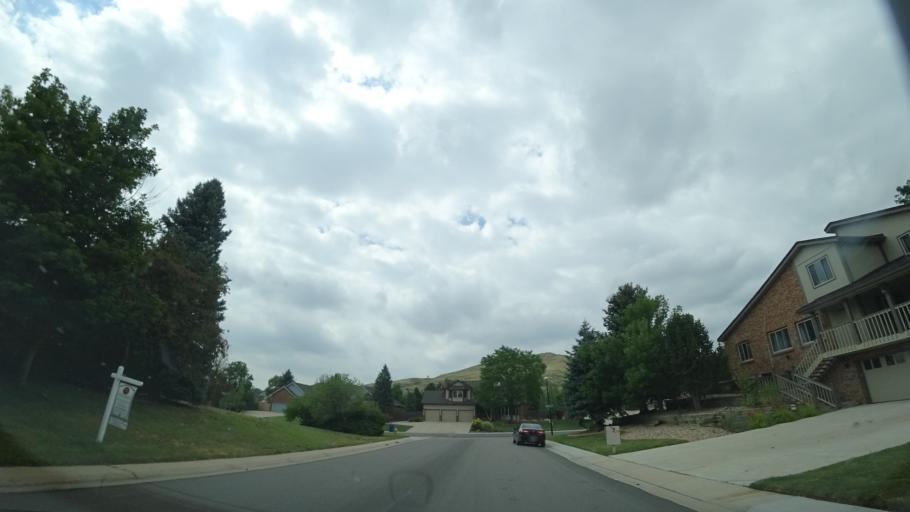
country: US
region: Colorado
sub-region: Jefferson County
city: West Pleasant View
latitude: 39.7126
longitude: -105.1647
